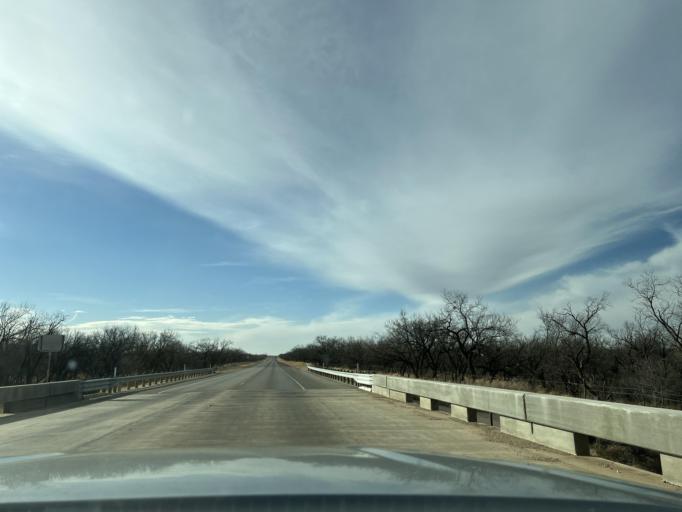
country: US
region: Texas
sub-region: Fisher County
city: Rotan
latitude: 32.7399
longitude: -100.5131
